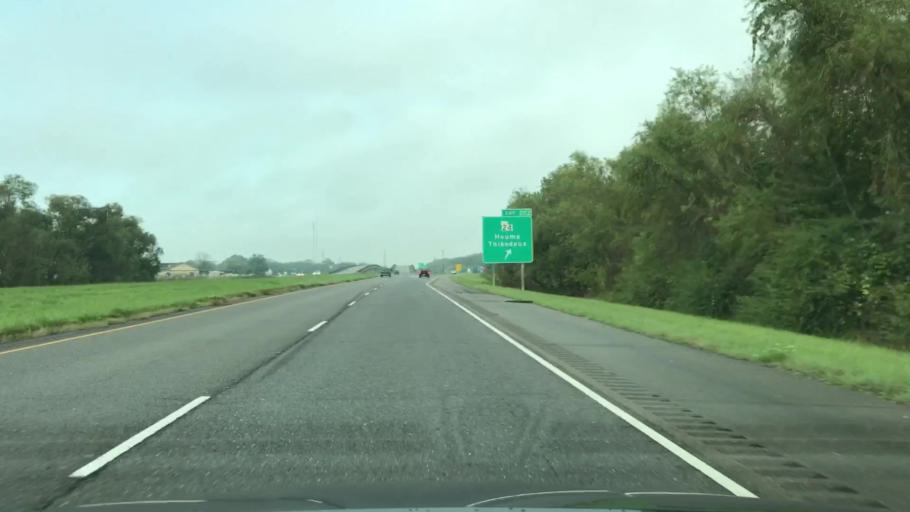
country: US
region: Louisiana
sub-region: Terrebonne Parish
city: Gray
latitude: 29.6805
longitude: -90.7758
